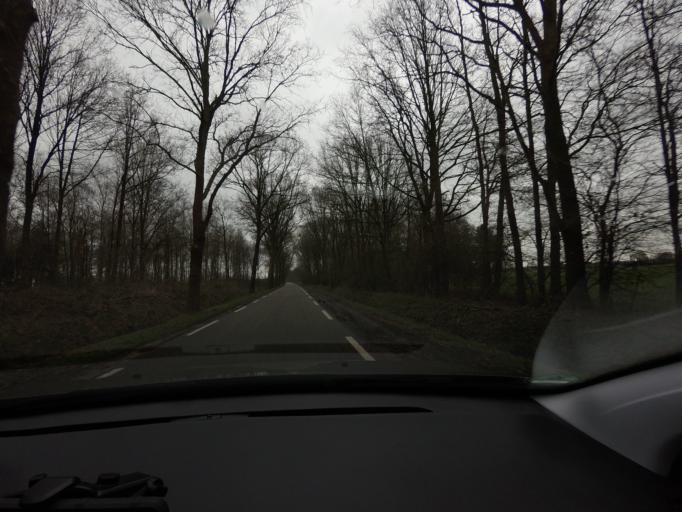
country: NL
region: Drenthe
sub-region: Gemeente Hoogeveen
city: Hoogeveen
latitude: 52.8000
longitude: 6.5174
